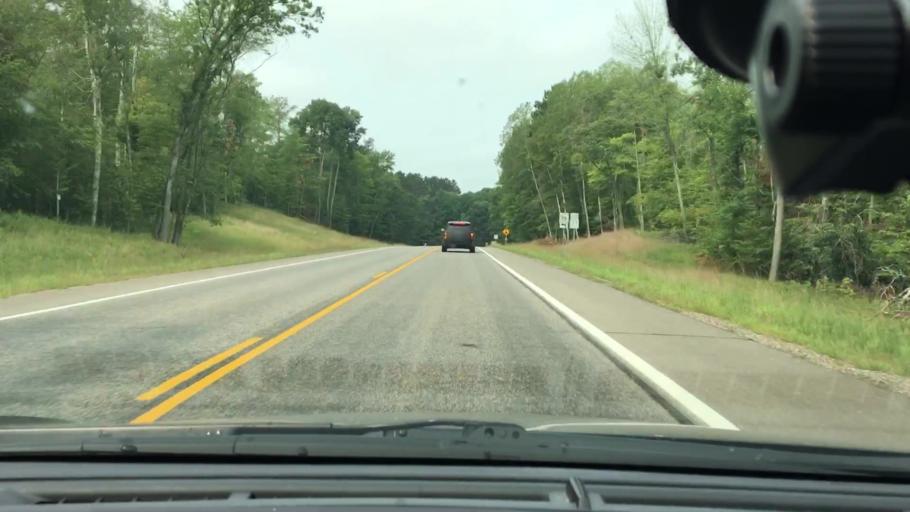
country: US
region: Minnesota
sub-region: Crow Wing County
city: Cross Lake
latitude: 46.6603
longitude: -94.0945
